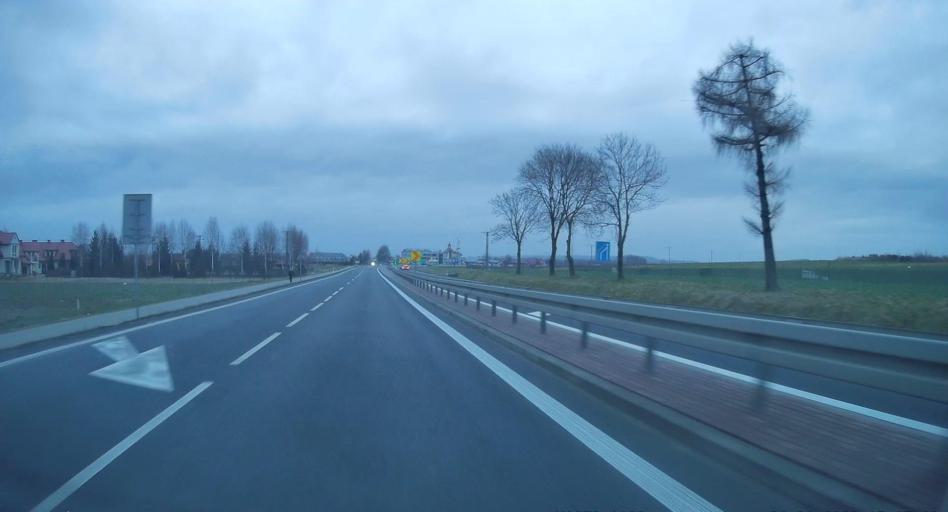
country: PL
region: Subcarpathian Voivodeship
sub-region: Powiat ropczycko-sedziszowski
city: Sedziszow Malopolski
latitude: 50.0688
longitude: 21.6728
